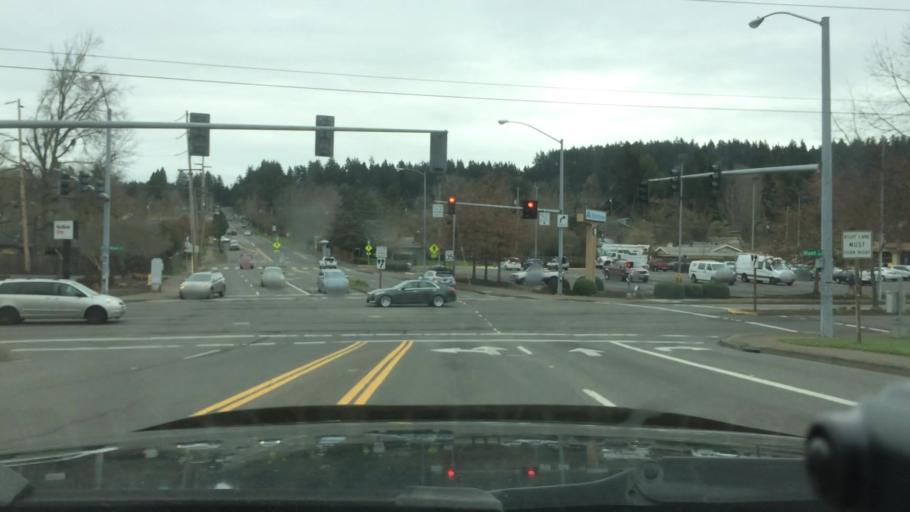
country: US
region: Oregon
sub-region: Lane County
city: Eugene
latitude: 44.0243
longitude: -123.0821
